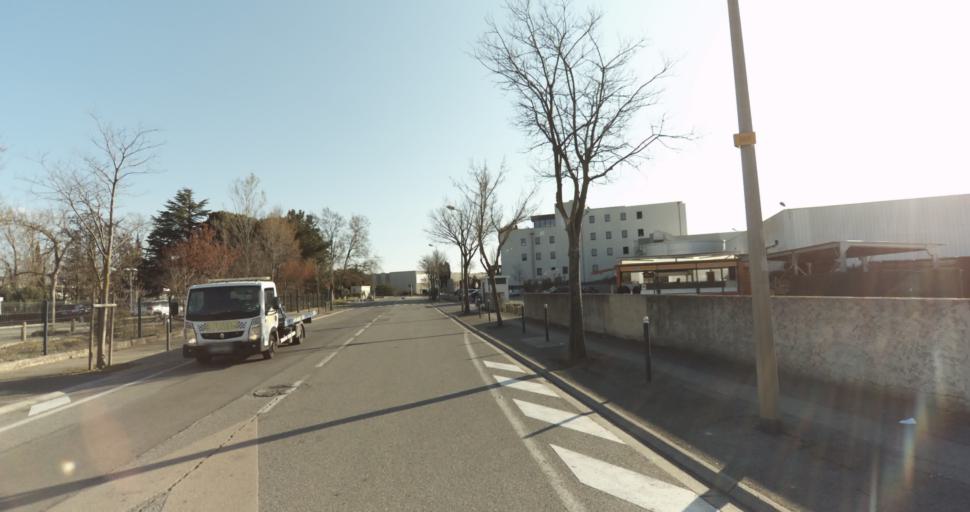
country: FR
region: Provence-Alpes-Cote d'Azur
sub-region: Departement des Bouches-du-Rhone
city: Cabries
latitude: 43.4926
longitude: 5.3737
